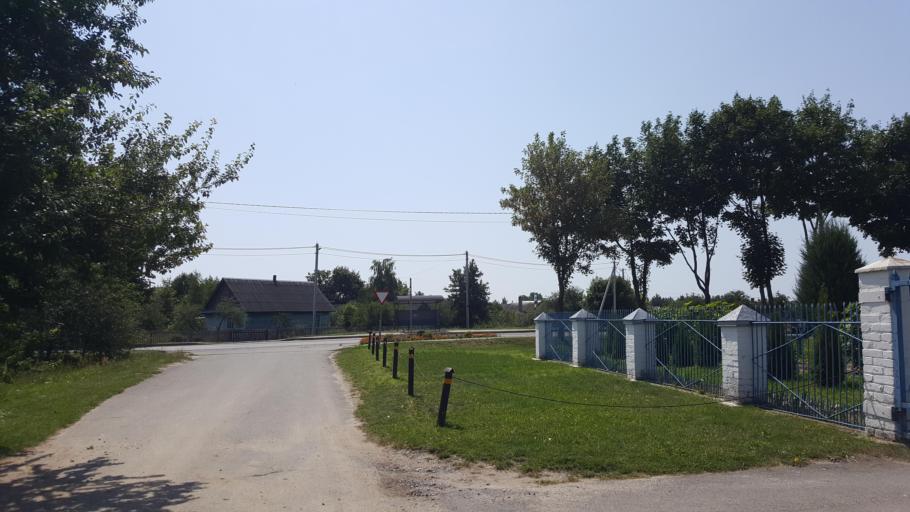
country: BY
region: Brest
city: Zhabinka
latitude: 52.1955
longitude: 23.9937
